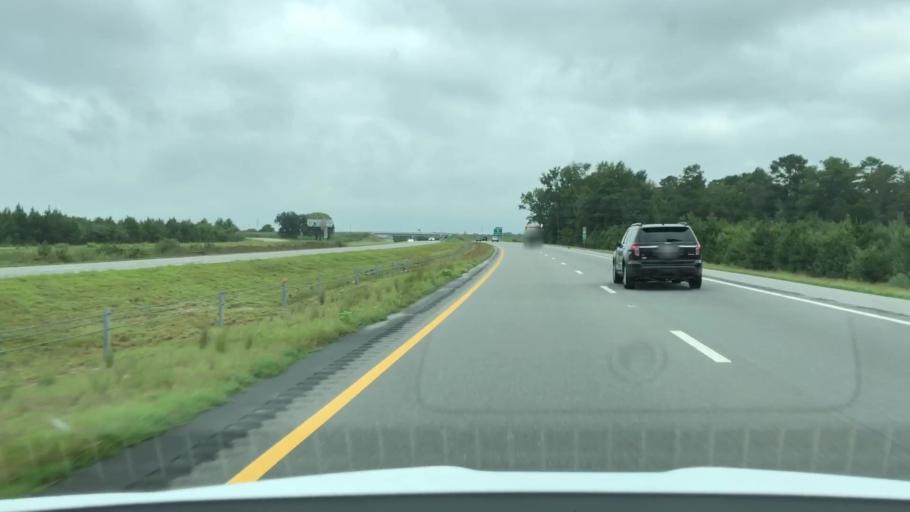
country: US
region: North Carolina
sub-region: Wayne County
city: Elroy
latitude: 35.4004
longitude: -77.8729
